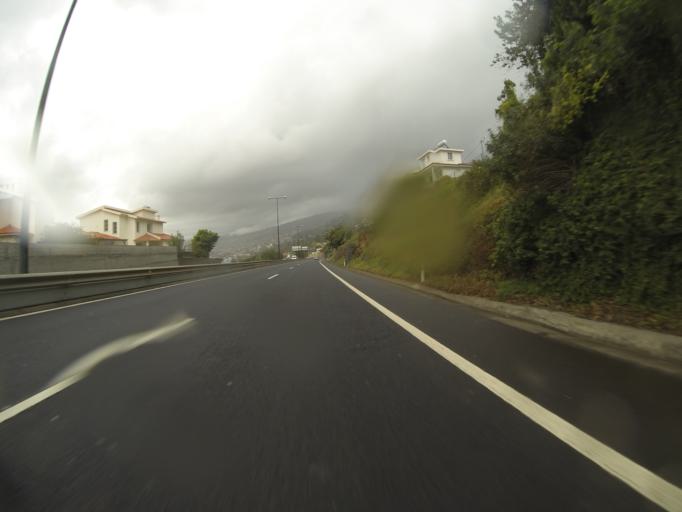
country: PT
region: Madeira
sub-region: Funchal
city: Nossa Senhora do Monte
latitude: 32.6589
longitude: -16.8888
